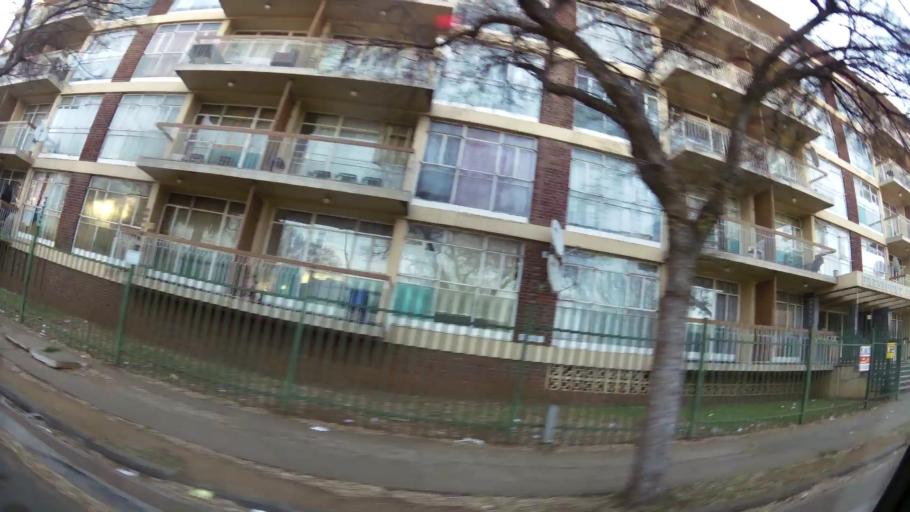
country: ZA
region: Gauteng
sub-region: Ekurhuleni Metropolitan Municipality
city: Germiston
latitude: -26.2613
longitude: 28.1279
